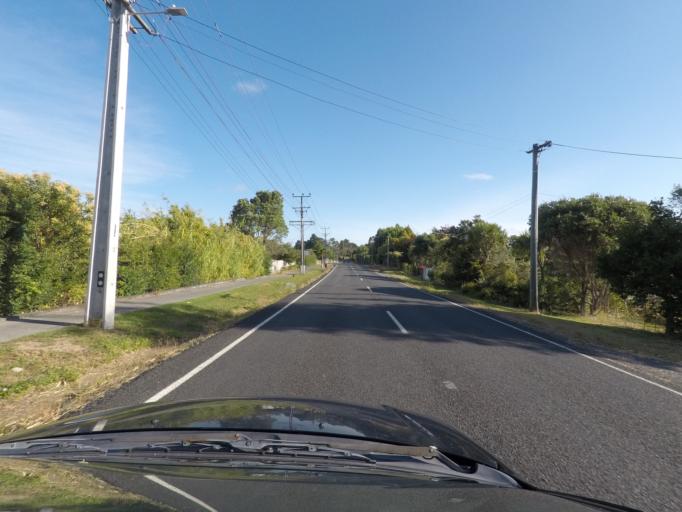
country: NZ
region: Auckland
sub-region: Auckland
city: Waitakere
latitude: -36.8783
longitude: 174.5975
